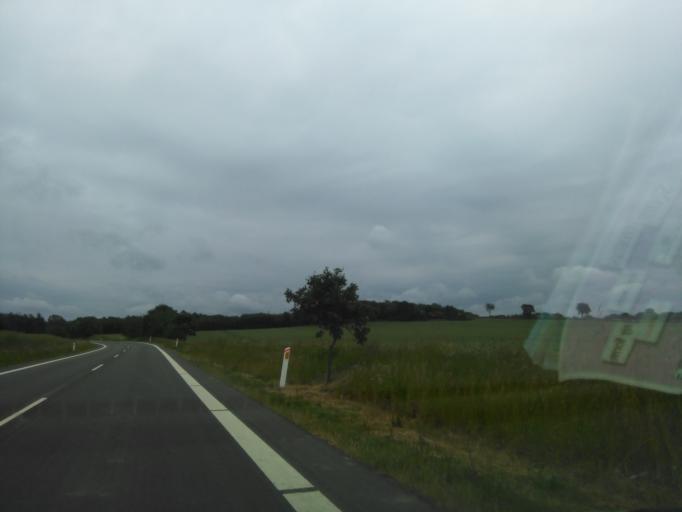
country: DK
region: Capital Region
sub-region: Bornholm Kommune
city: Akirkeby
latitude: 55.1174
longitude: 14.8311
